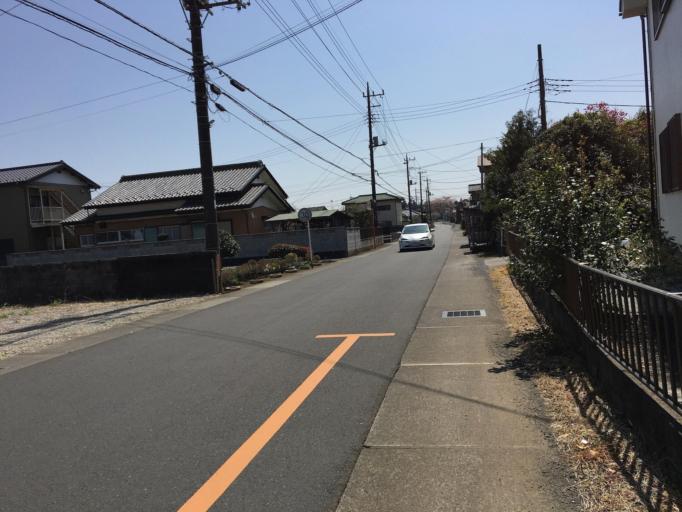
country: JP
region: Saitama
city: Sakado
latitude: 35.8986
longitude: 139.3640
